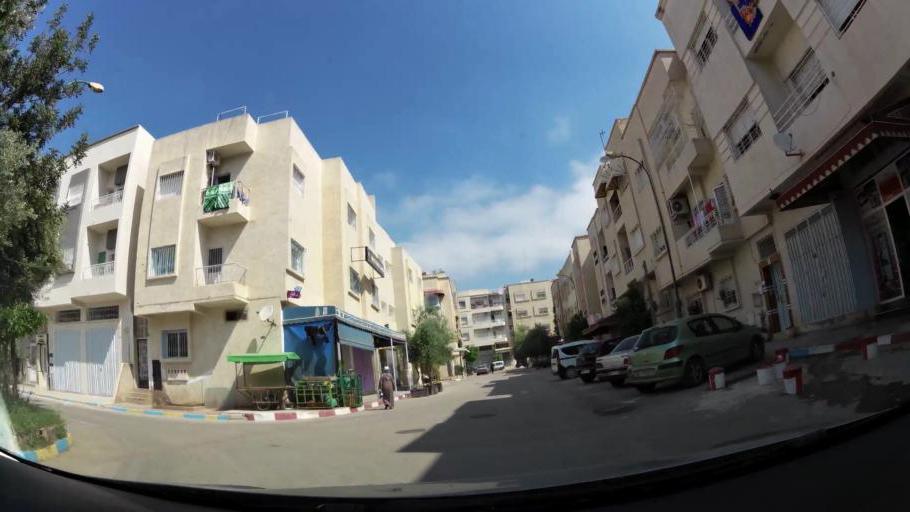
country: MA
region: Fes-Boulemane
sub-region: Fes
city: Fes
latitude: 34.0560
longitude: -5.0293
